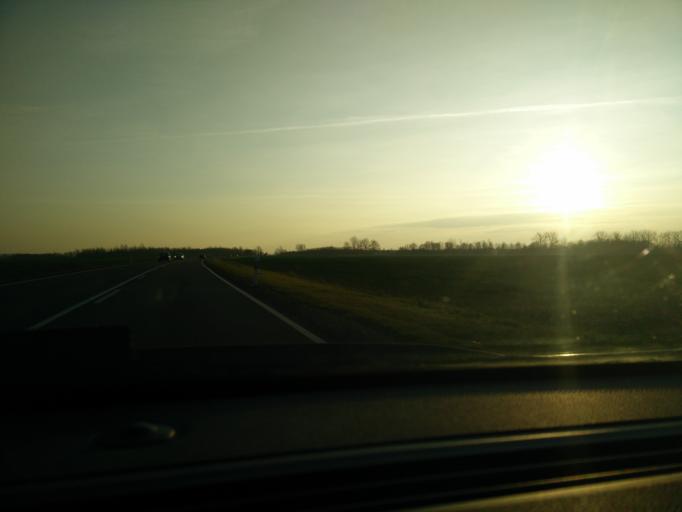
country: DE
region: Saxony
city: Grossposna
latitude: 51.2416
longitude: 12.4885
